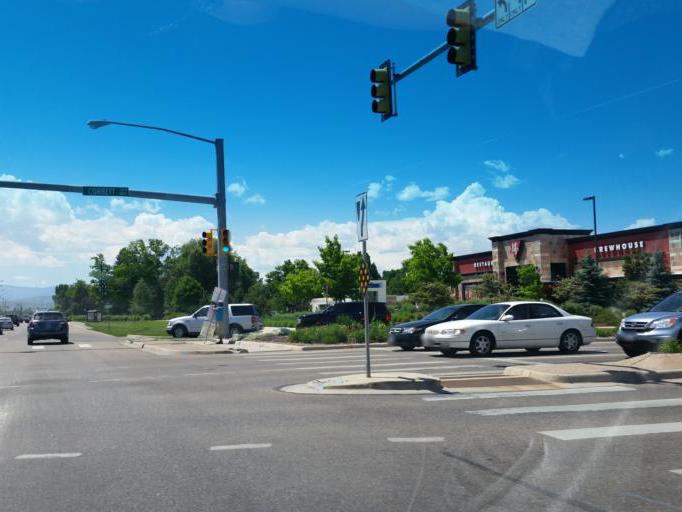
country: US
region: Colorado
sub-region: Larimer County
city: Fort Collins
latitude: 40.5234
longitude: -105.0268
